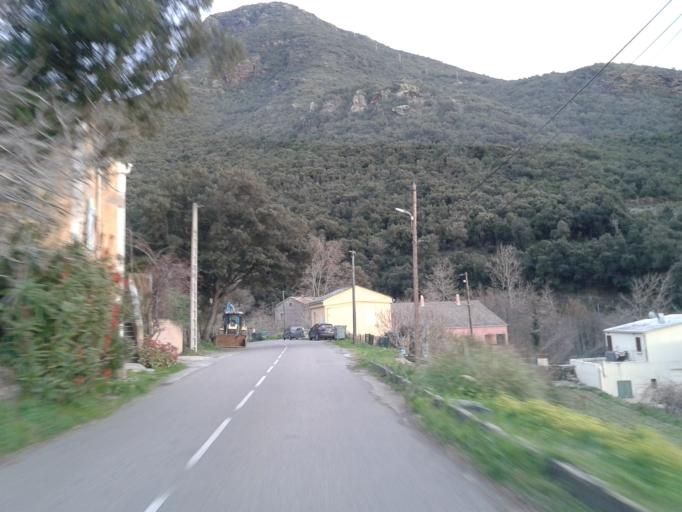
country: FR
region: Corsica
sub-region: Departement de la Haute-Corse
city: Santa-Maria-di-Lota
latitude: 42.7614
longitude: 9.3454
